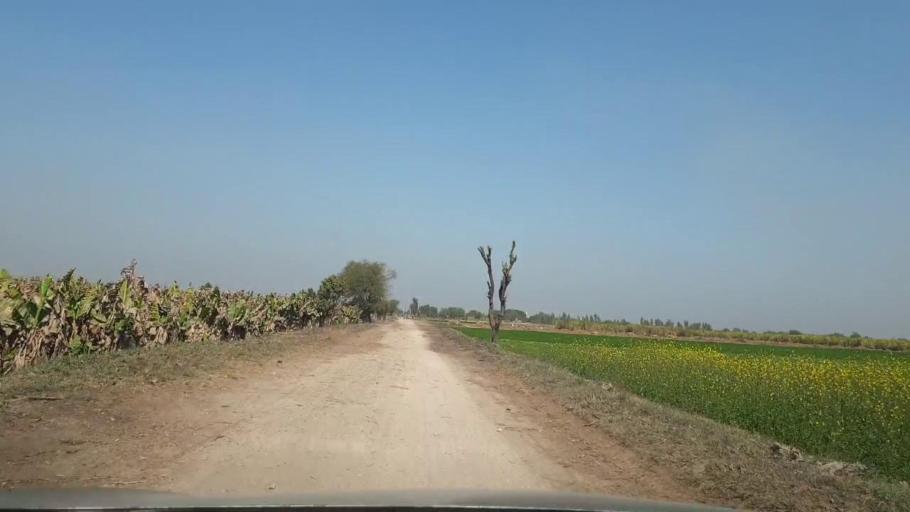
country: PK
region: Sindh
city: Tando Allahyar
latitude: 25.6039
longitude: 68.6423
